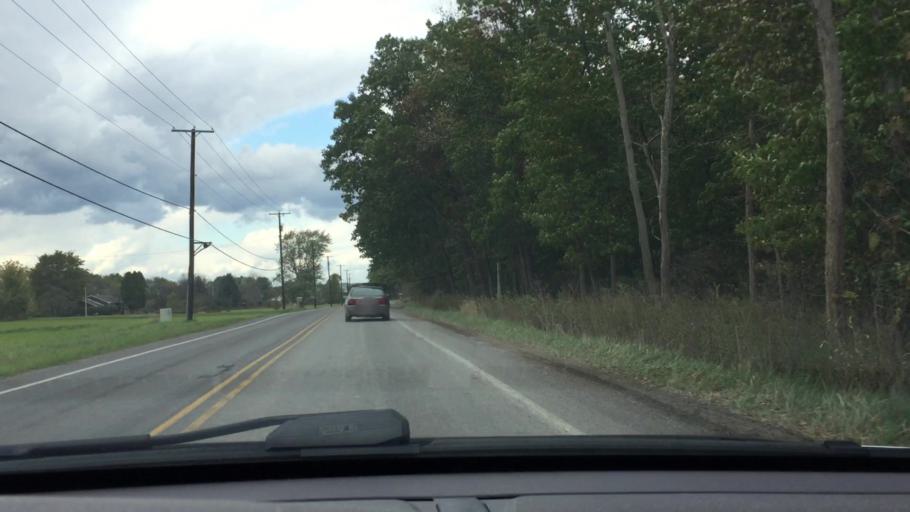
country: US
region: Pennsylvania
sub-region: Lawrence County
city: Bessemer
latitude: 40.9935
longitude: -80.4371
